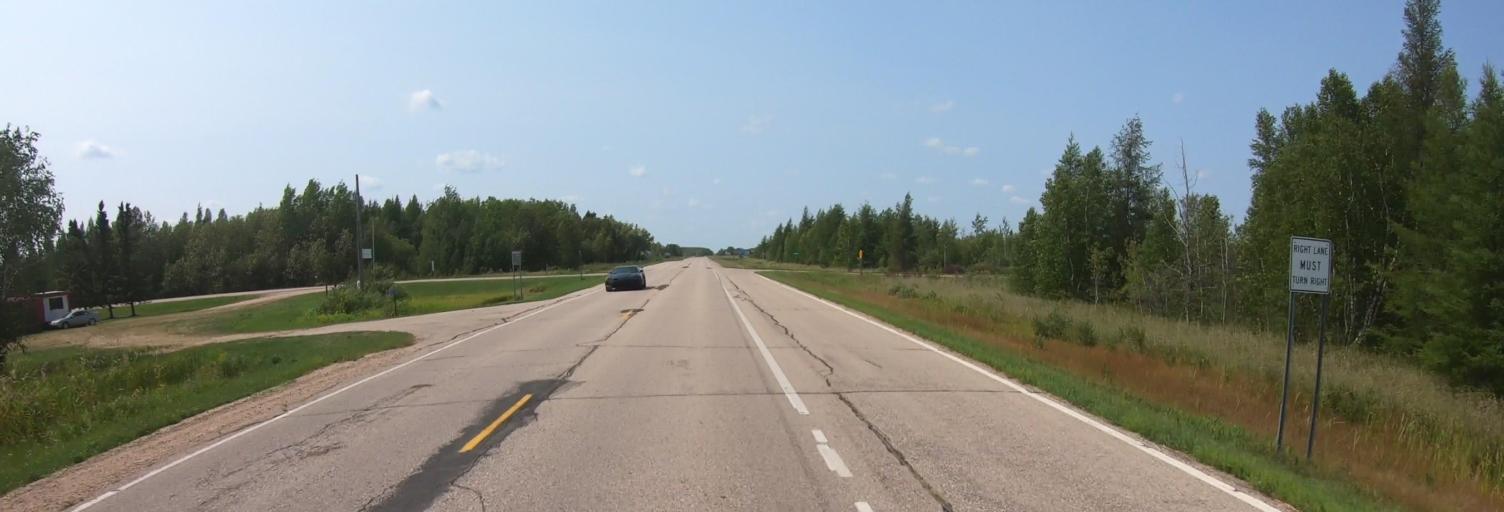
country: US
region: Minnesota
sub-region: Lake of the Woods County
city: Baudette
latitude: 48.7395
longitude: -94.8363
